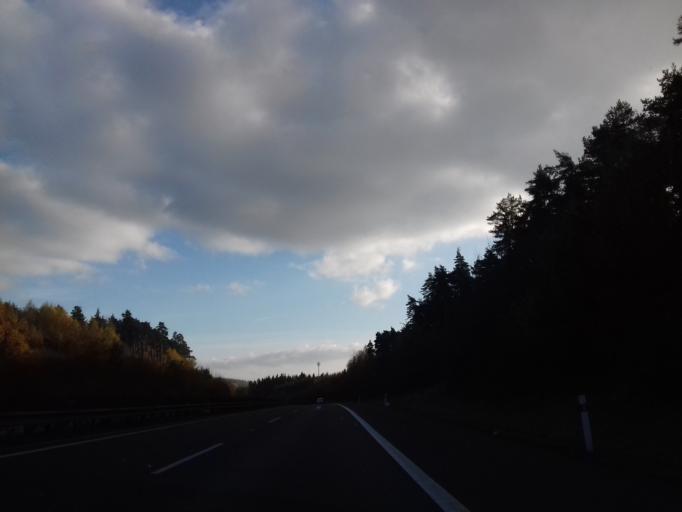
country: CZ
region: Plzensky
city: Dobrany
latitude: 49.6856
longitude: 13.3010
